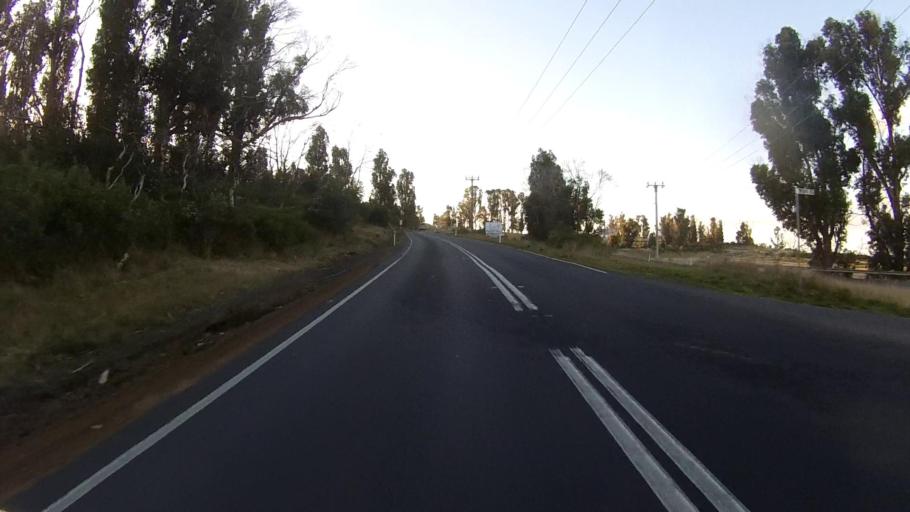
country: AU
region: Tasmania
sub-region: Sorell
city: Sorell
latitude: -42.8766
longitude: 147.8233
